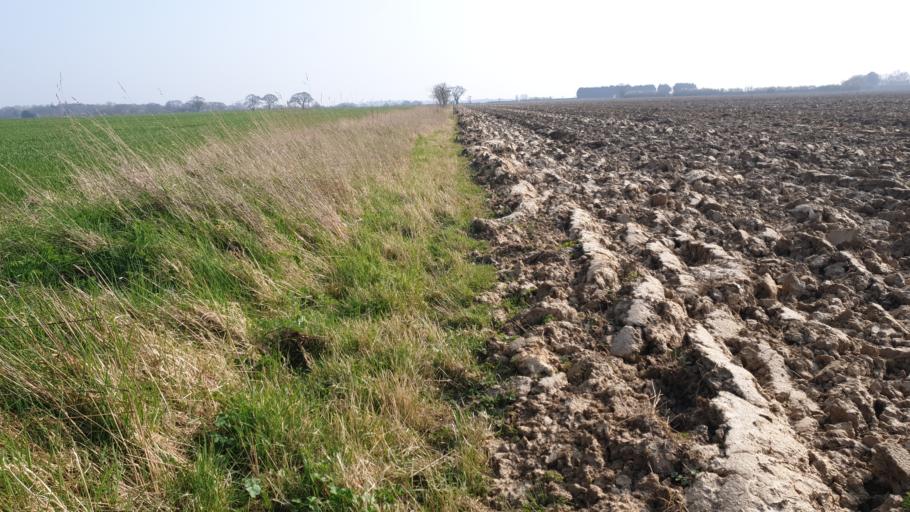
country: GB
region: England
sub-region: Essex
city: Mistley
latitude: 51.9067
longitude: 1.1272
